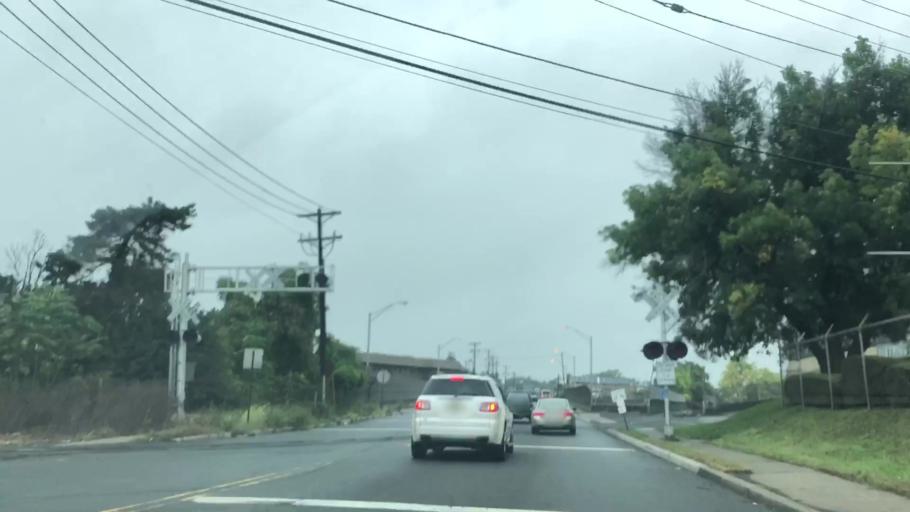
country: US
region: New Jersey
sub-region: Union County
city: Hillside
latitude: 40.7063
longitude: -74.2333
